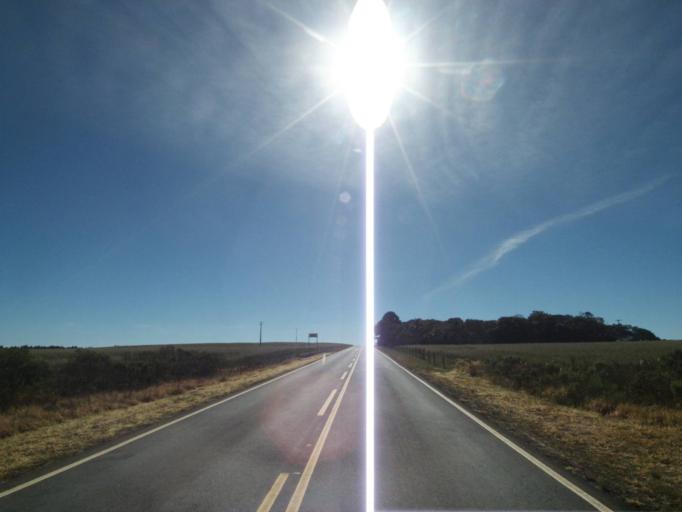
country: BR
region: Parana
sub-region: Castro
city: Castro
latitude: -24.7076
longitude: -50.1940
